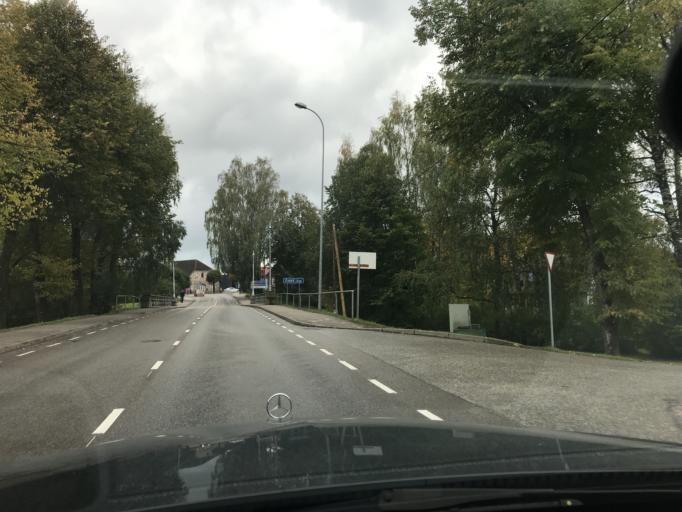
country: EE
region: Valgamaa
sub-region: Torva linn
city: Torva
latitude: 58.0041
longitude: 25.9205
